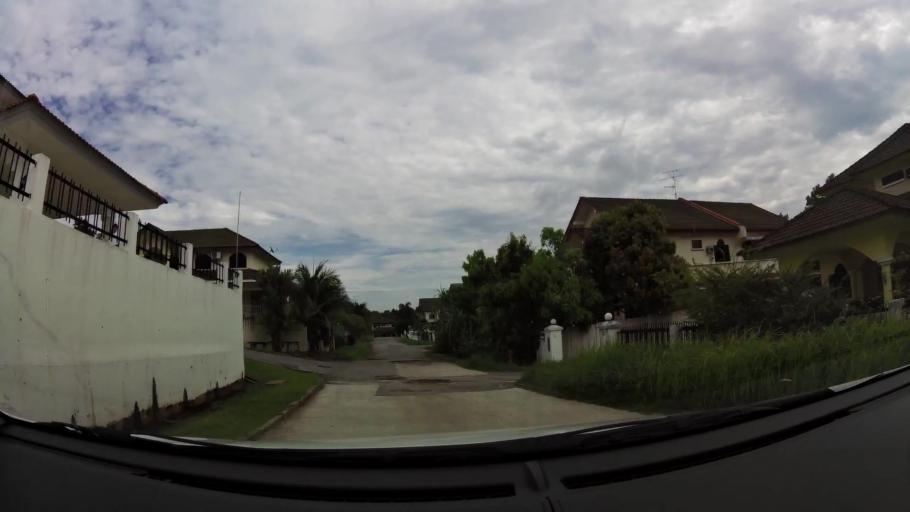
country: BN
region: Brunei and Muara
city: Bandar Seri Begawan
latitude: 4.8858
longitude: 114.8988
